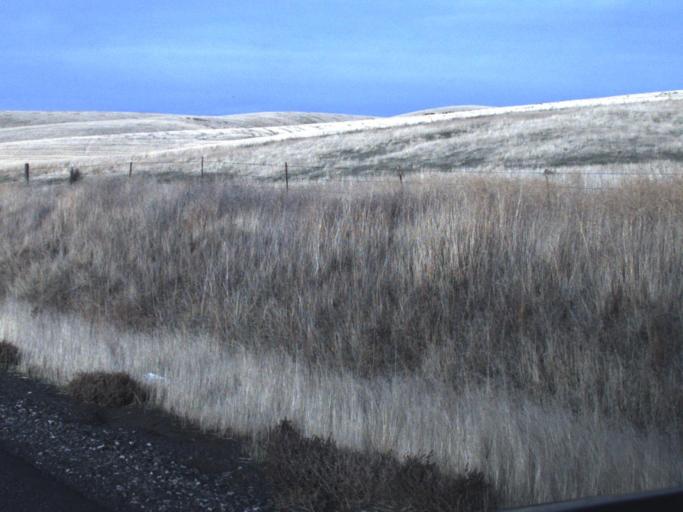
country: US
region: Washington
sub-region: Garfield County
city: Pomeroy
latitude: 46.5025
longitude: -117.7760
